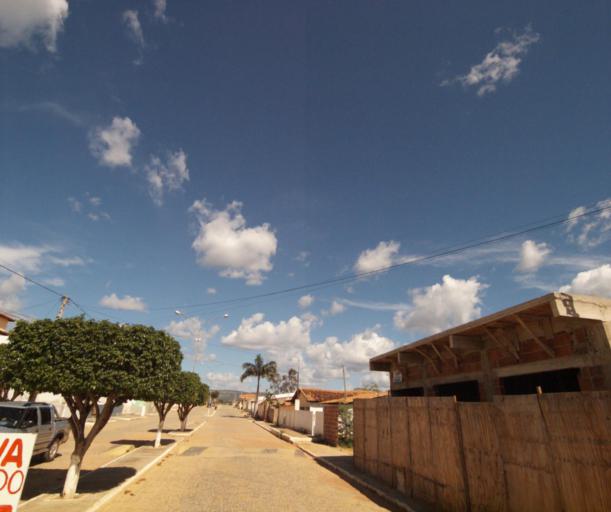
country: BR
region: Bahia
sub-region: Pocoes
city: Pocoes
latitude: -14.2421
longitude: -40.7664
